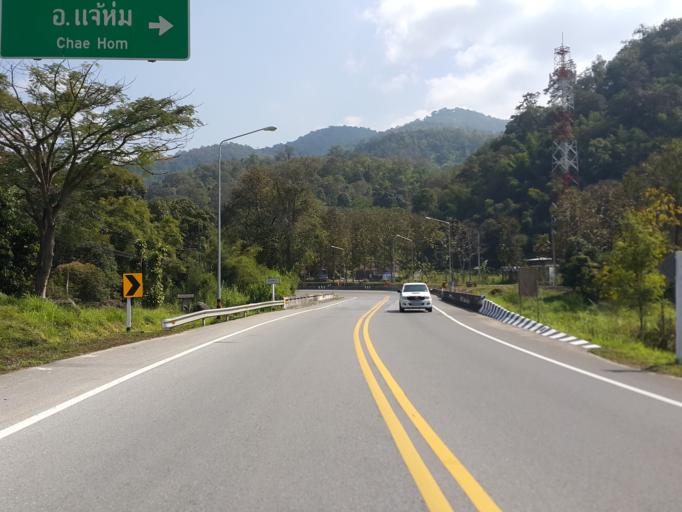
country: TH
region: Chiang Mai
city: Mae On
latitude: 19.0163
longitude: 99.3025
